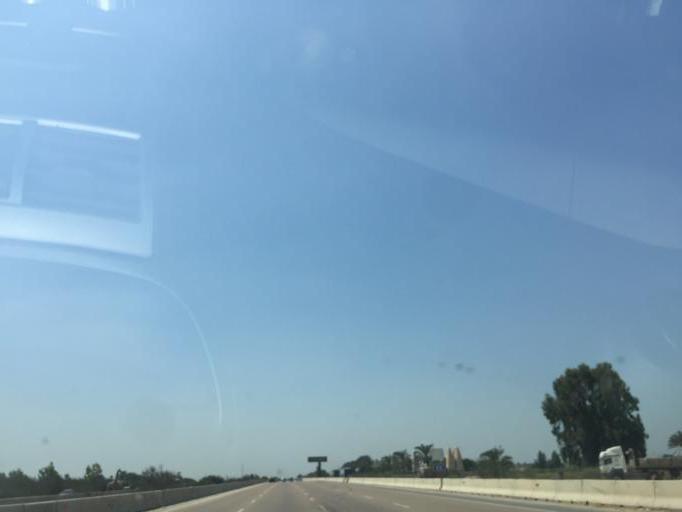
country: EG
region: Al Buhayrah
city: Abu al Matamir
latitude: 30.7631
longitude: 29.9832
